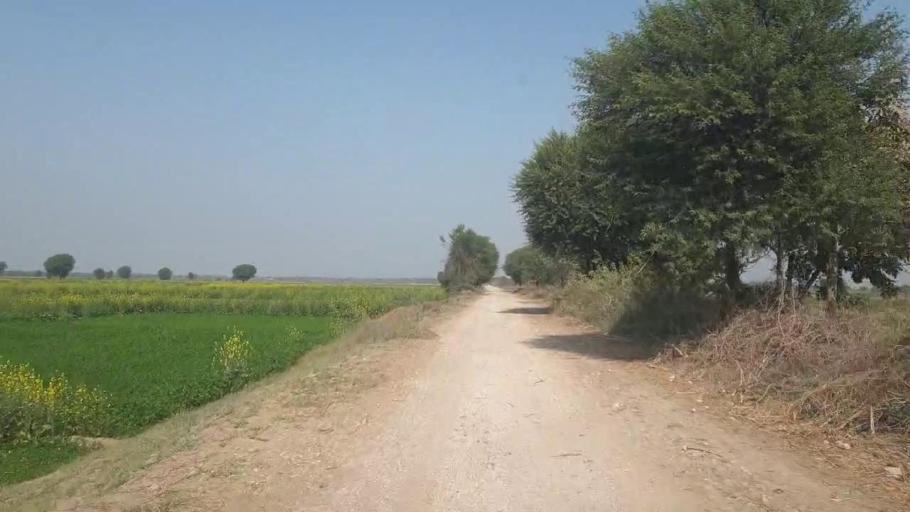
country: PK
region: Sindh
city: Tando Allahyar
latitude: 25.4570
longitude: 68.8319
